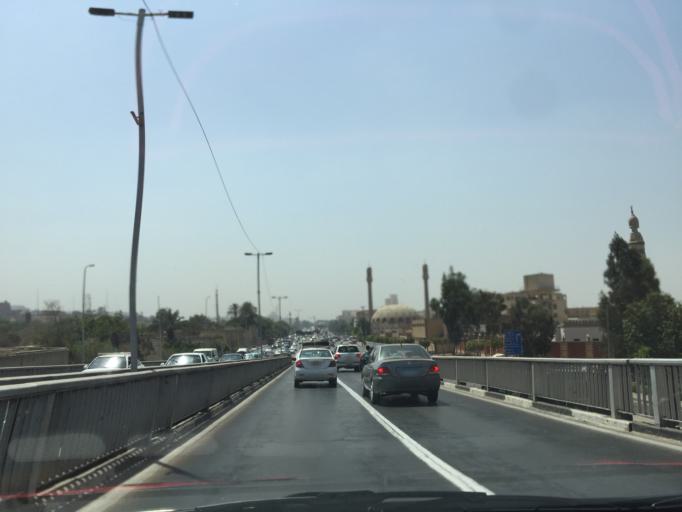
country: EG
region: Muhafazat al Qahirah
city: Cairo
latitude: 30.0545
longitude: 31.2789
